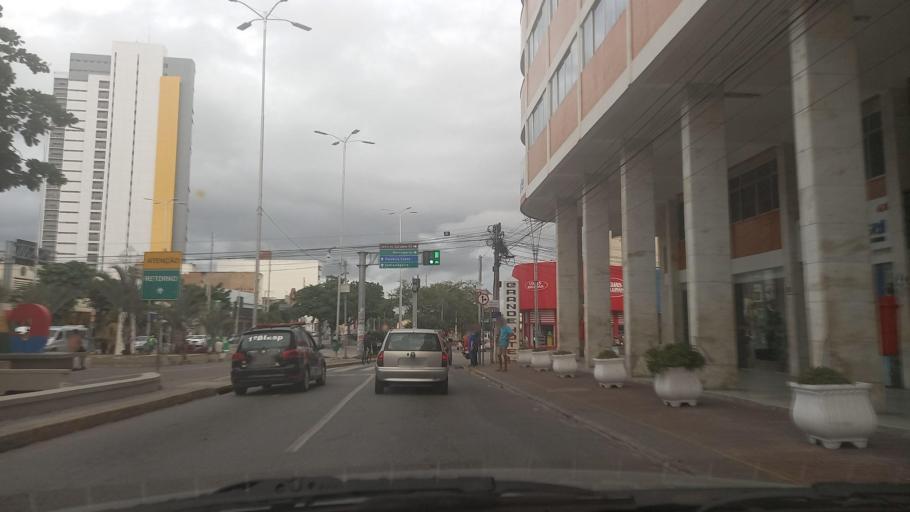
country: BR
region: Pernambuco
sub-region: Caruaru
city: Caruaru
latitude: -8.2825
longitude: -35.9720
